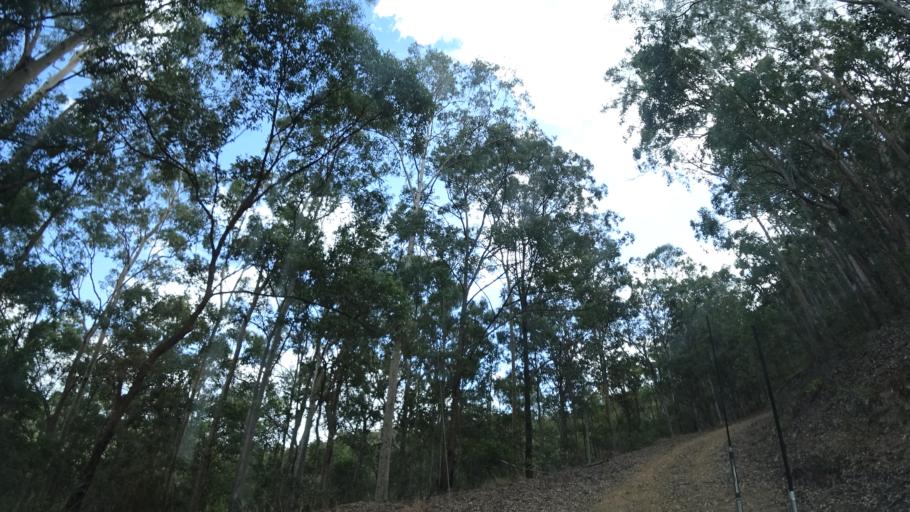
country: AU
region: Queensland
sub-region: Moreton Bay
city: Highvale
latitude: -27.3450
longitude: 152.7278
